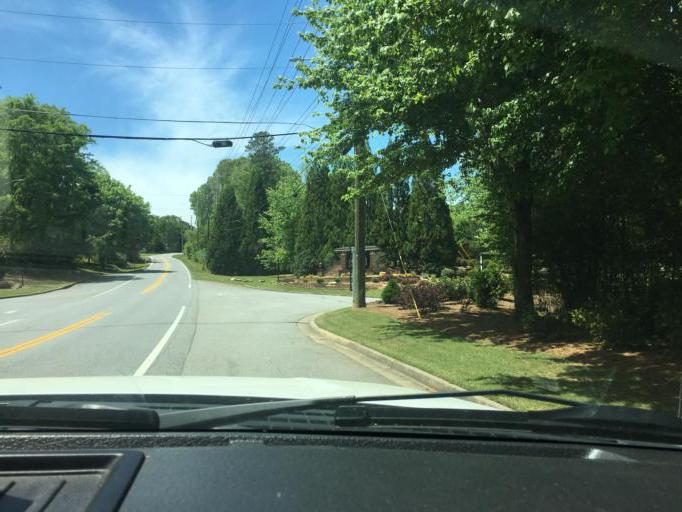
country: US
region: Georgia
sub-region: Fulton County
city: Milton
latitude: 34.1227
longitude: -84.3983
